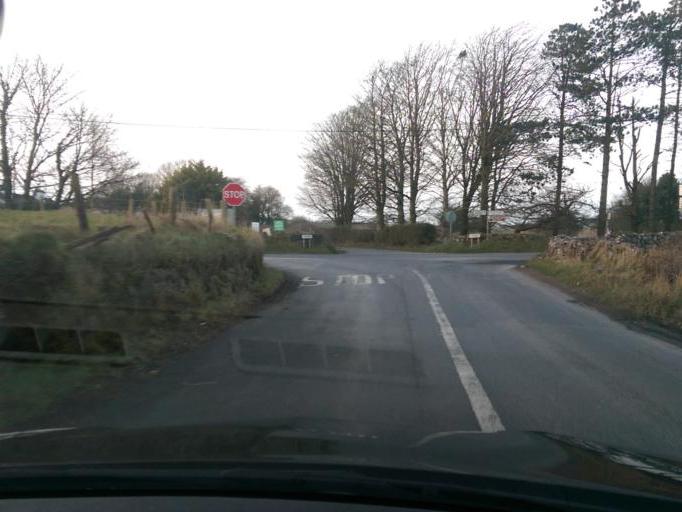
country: IE
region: Connaught
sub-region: County Galway
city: Athenry
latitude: 53.2717
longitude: -8.6942
